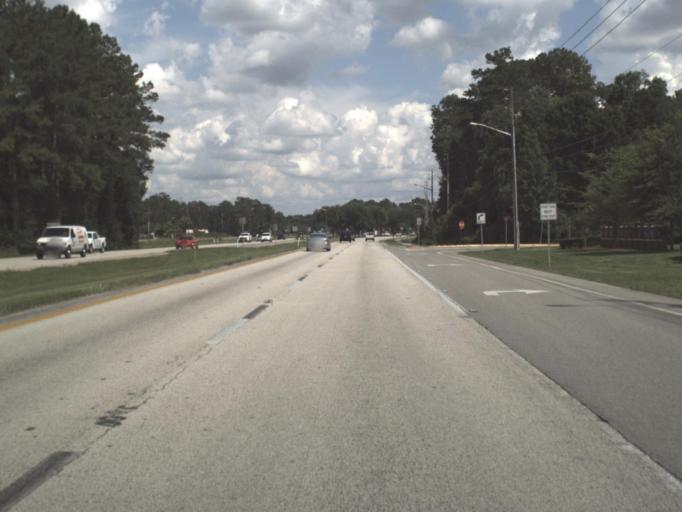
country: US
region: Florida
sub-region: Alachua County
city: Gainesville
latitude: 29.7022
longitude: -82.3426
